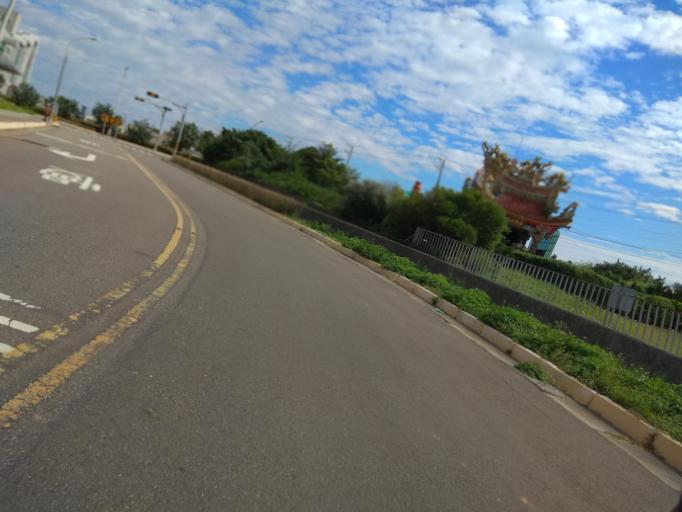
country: TW
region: Taiwan
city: Taoyuan City
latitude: 25.0525
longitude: 121.0957
